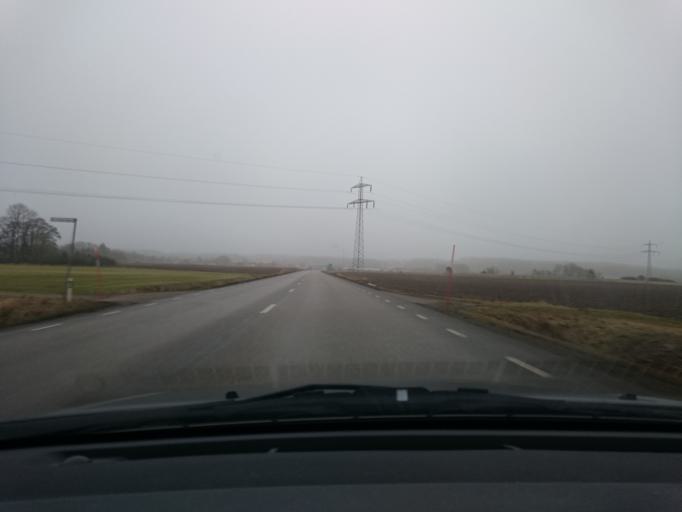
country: SE
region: Skane
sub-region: Angelholms Kommun
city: AEngelholm
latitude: 56.3171
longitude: 12.9014
